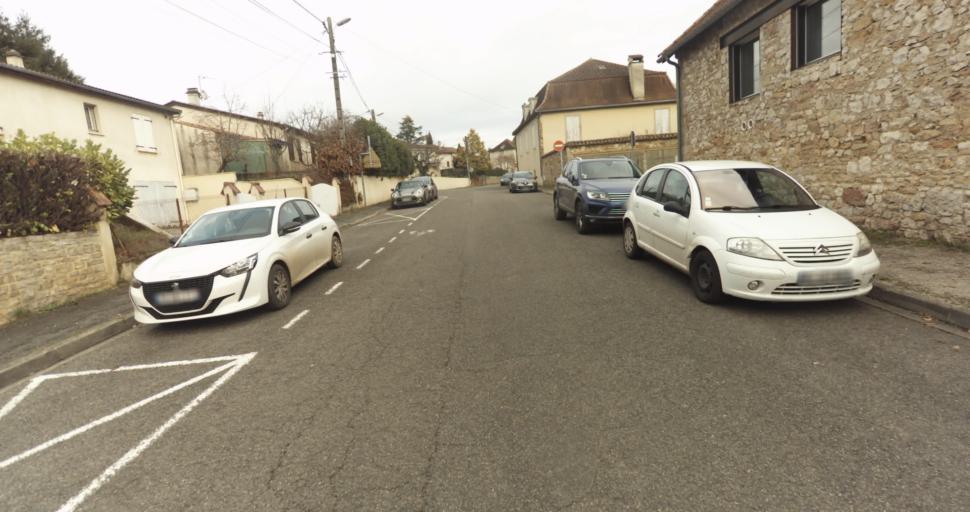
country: FR
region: Midi-Pyrenees
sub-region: Departement du Lot
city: Figeac
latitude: 44.6102
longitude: 2.0204
